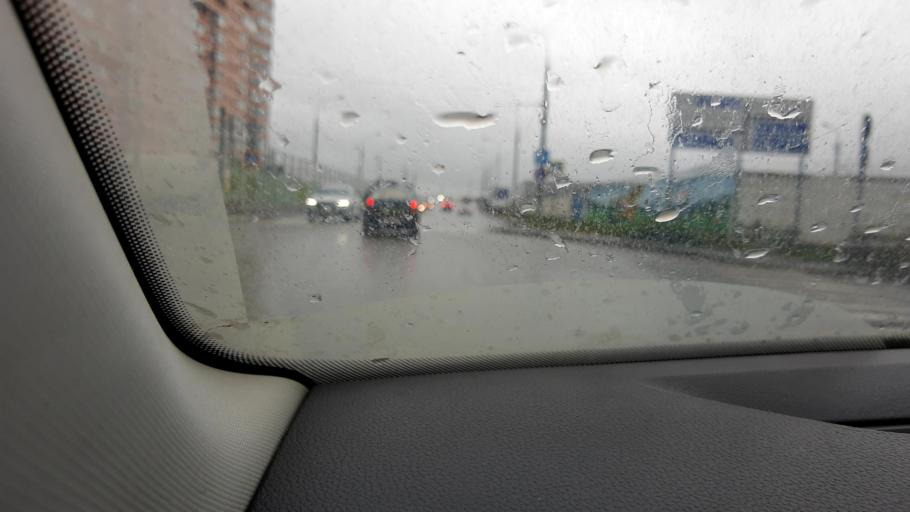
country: RU
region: Moskovskaya
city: Aprelevka
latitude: 55.5407
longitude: 37.0773
